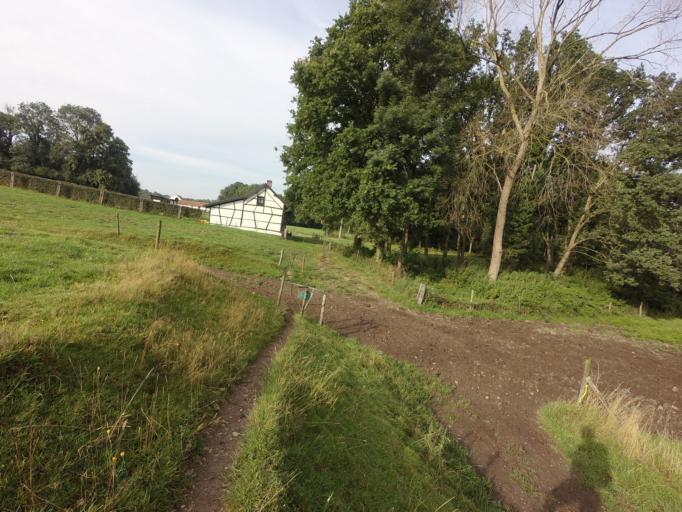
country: NL
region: Limburg
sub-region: Eijsden-Margraten
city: Margraten
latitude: 50.7913
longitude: 5.8620
